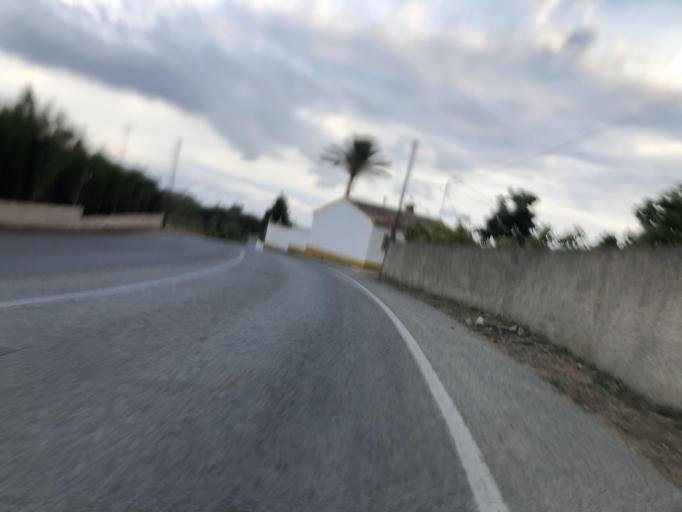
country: ES
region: Valencia
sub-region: Provincia de Alicante
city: Polop
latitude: 38.6275
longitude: -0.1401
